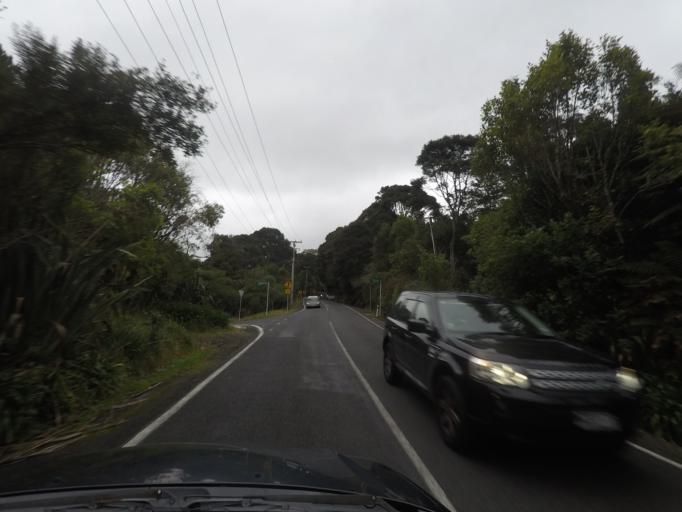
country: NZ
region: Auckland
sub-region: Auckland
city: Titirangi
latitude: -36.9321
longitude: 174.5808
